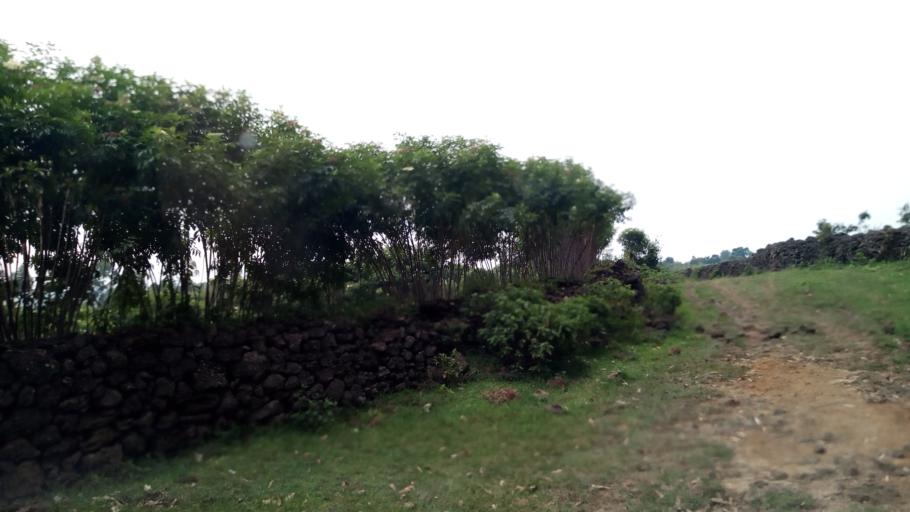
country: UG
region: Western Region
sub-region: Kisoro District
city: Kisoro
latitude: -1.2647
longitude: 29.6058
